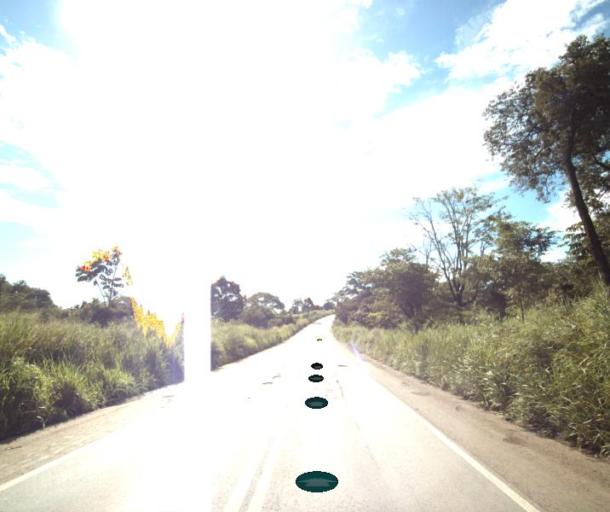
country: BR
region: Goias
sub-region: Jaragua
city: Jaragua
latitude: -15.6119
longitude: -49.4016
